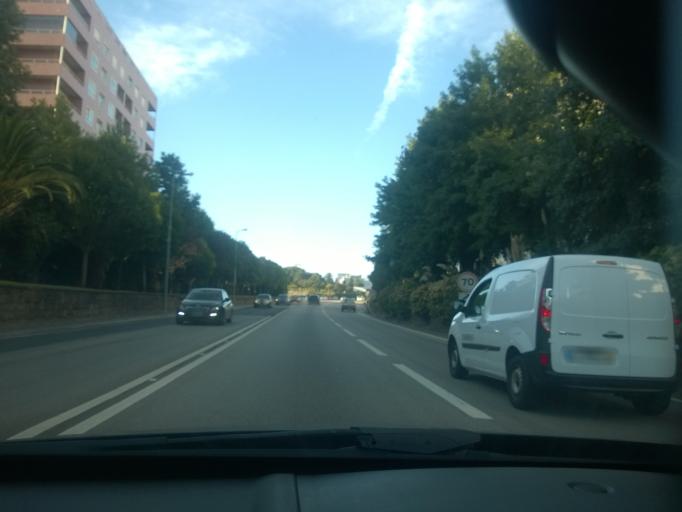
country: PT
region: Porto
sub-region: Maia
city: Maia
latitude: 41.2336
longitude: -8.6270
